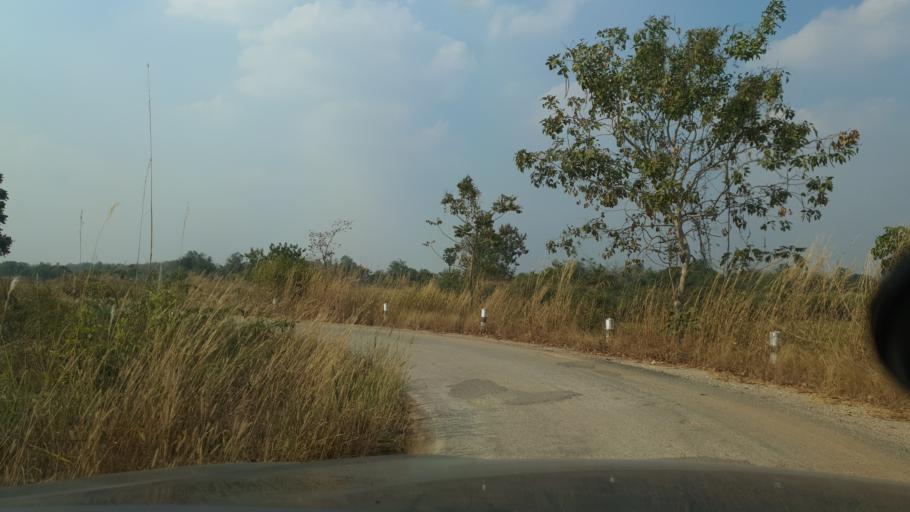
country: TH
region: Sukhothai
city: Ban Dan Lan Hoi
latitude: 17.0208
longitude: 99.5557
